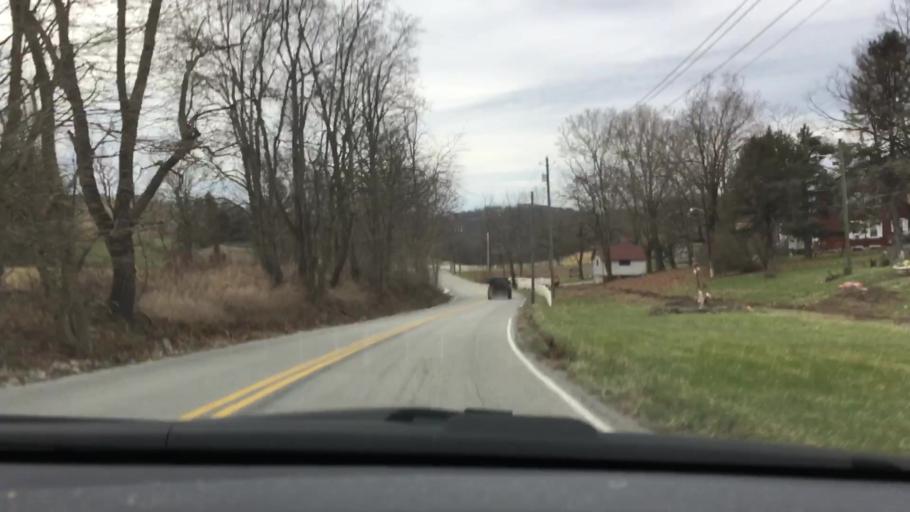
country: US
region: Pennsylvania
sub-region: Washington County
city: Midland
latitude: 40.2781
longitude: -80.2173
